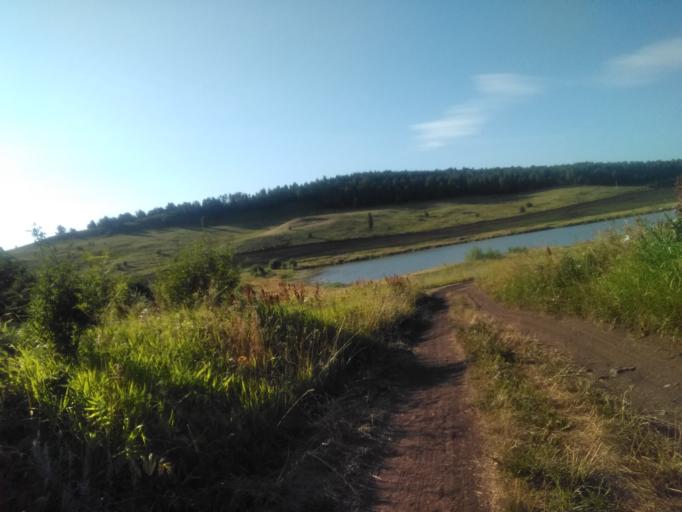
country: RU
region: Tatarstan
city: Russkiy Aktash
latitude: 54.8795
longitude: 52.0737
